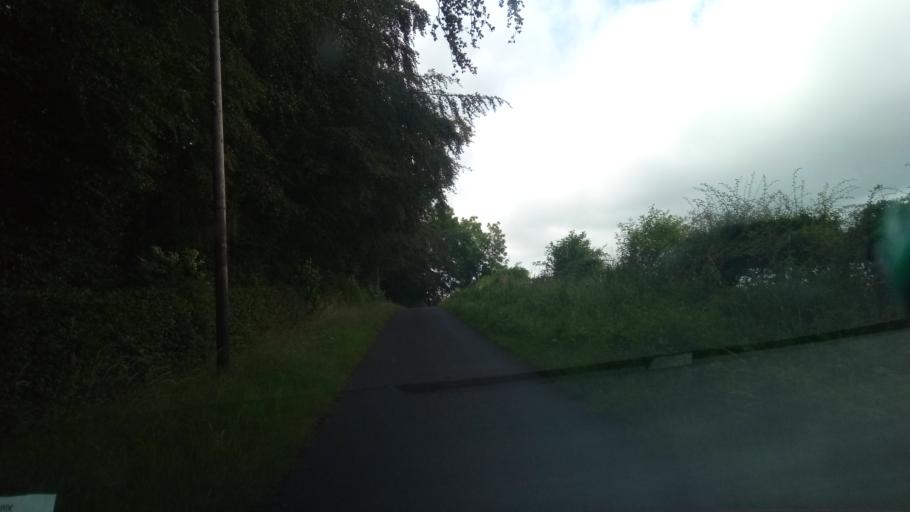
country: GB
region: Scotland
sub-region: The Scottish Borders
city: Hawick
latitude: 55.4389
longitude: -2.6943
